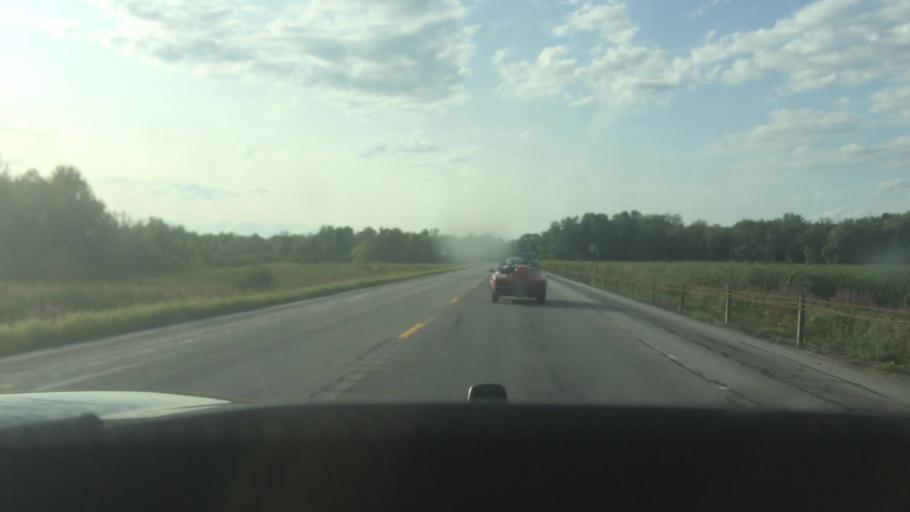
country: US
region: New York
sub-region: St. Lawrence County
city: Canton
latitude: 44.6156
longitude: -75.2194
